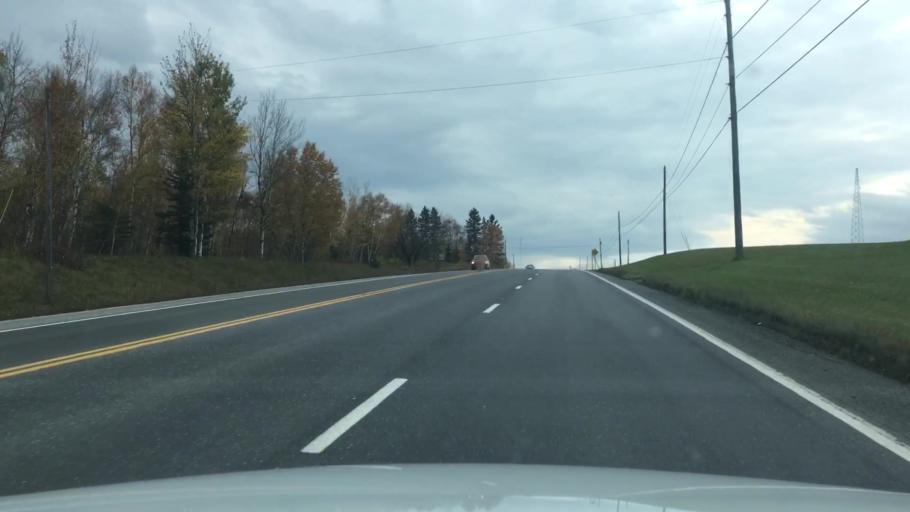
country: US
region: Maine
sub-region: Aroostook County
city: Caribou
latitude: 46.7813
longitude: -67.9891
